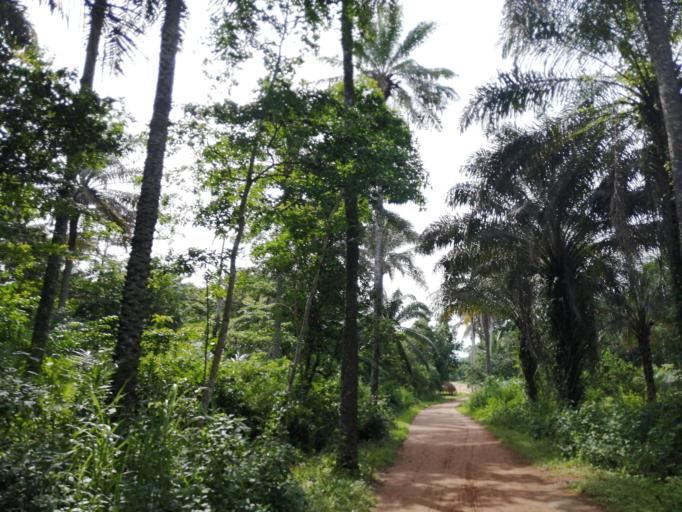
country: SL
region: Northern Province
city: Port Loko
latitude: 8.7900
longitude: -12.9304
